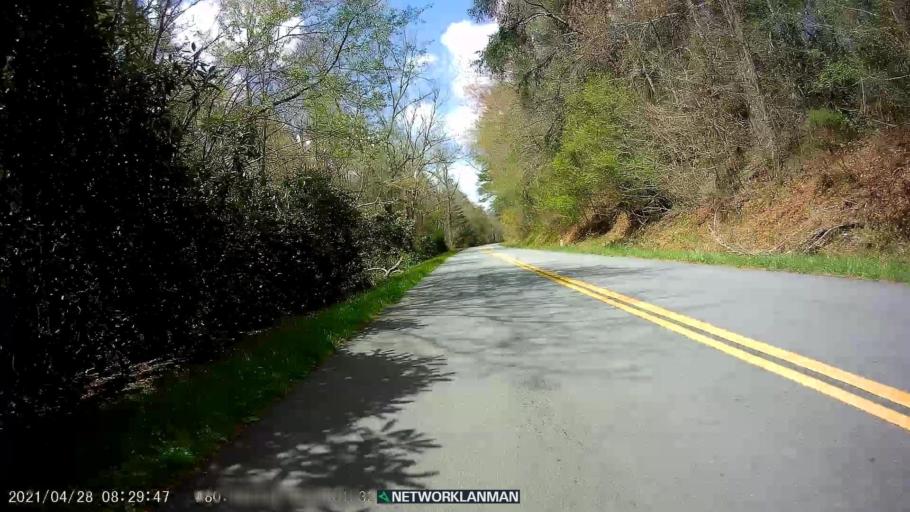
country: US
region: North Carolina
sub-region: Surry County
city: Thurmond
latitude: 36.4617
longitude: -80.9921
